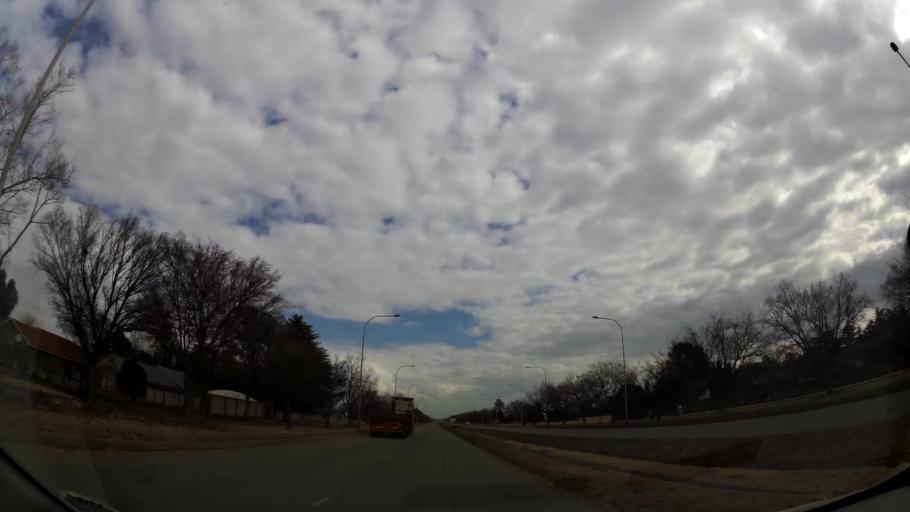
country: ZA
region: Gauteng
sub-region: Sedibeng District Municipality
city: Vereeniging
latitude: -26.6517
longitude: 27.9964
